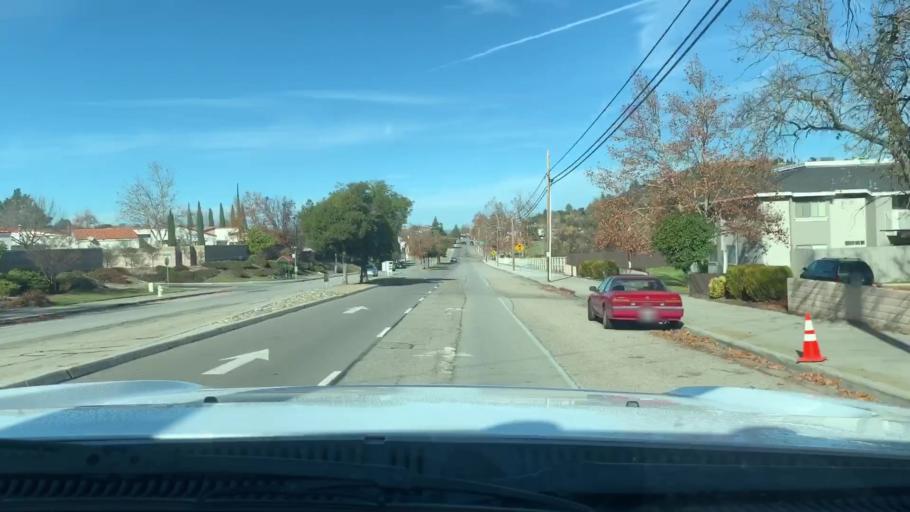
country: US
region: California
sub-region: San Luis Obispo County
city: Atascadero
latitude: 35.4582
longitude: -120.6419
